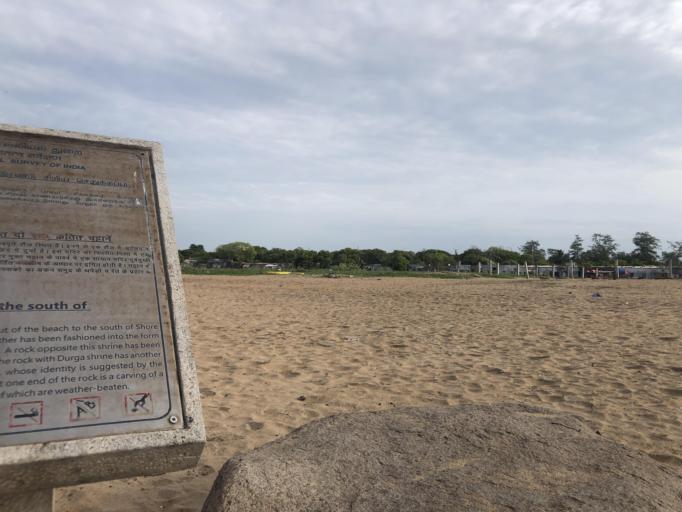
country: IN
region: Tamil Nadu
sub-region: Kancheepuram
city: Mamallapuram
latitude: 12.6145
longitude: 80.1979
